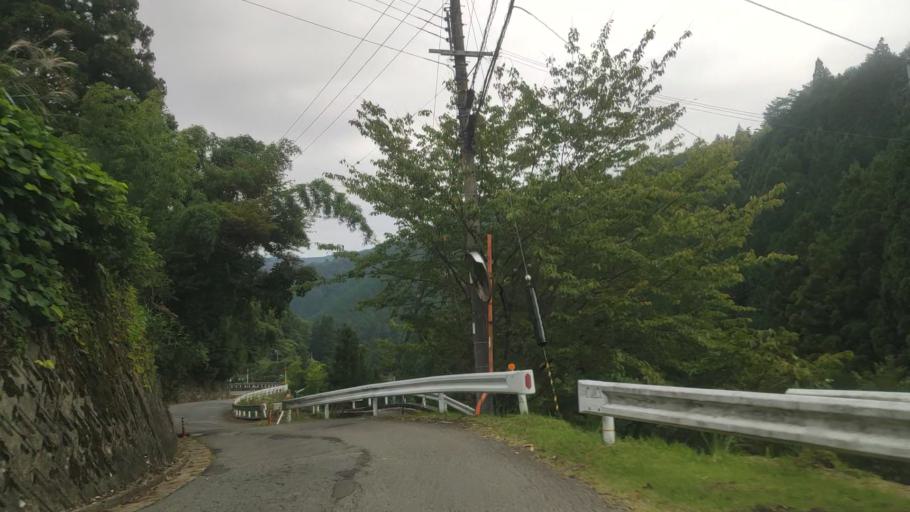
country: JP
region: Wakayama
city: Koya
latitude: 34.2275
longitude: 135.6203
